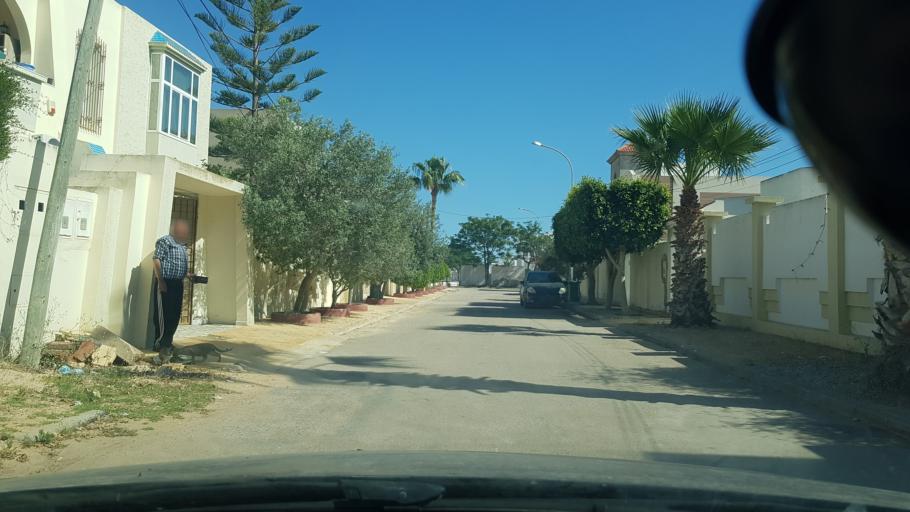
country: TN
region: Safaqis
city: Al Qarmadah
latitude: 34.8299
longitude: 10.7586
